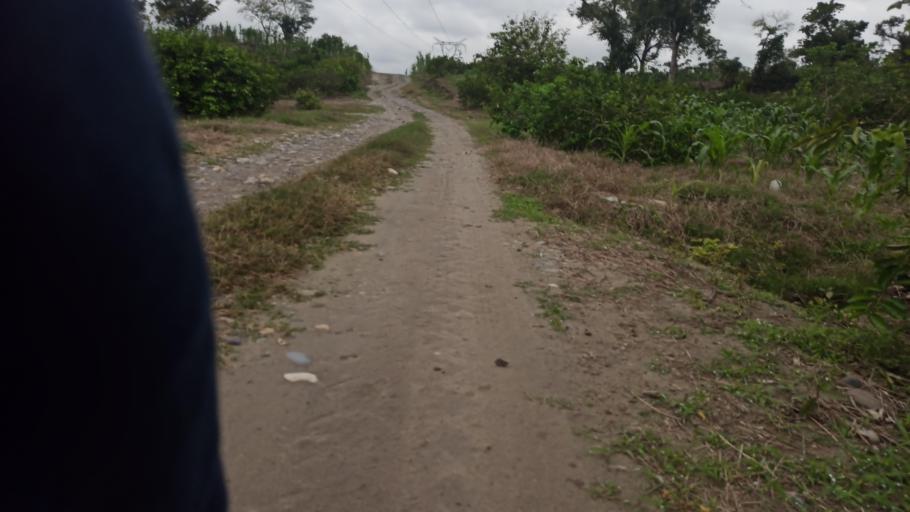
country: MX
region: Puebla
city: Espinal
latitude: 20.2952
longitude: -97.3996
